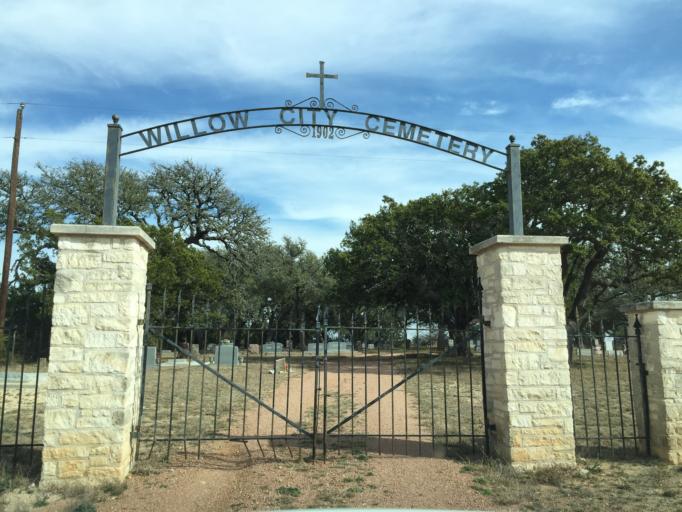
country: US
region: Texas
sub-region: Gillespie County
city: Fredericksburg
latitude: 30.3912
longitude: -98.7068
